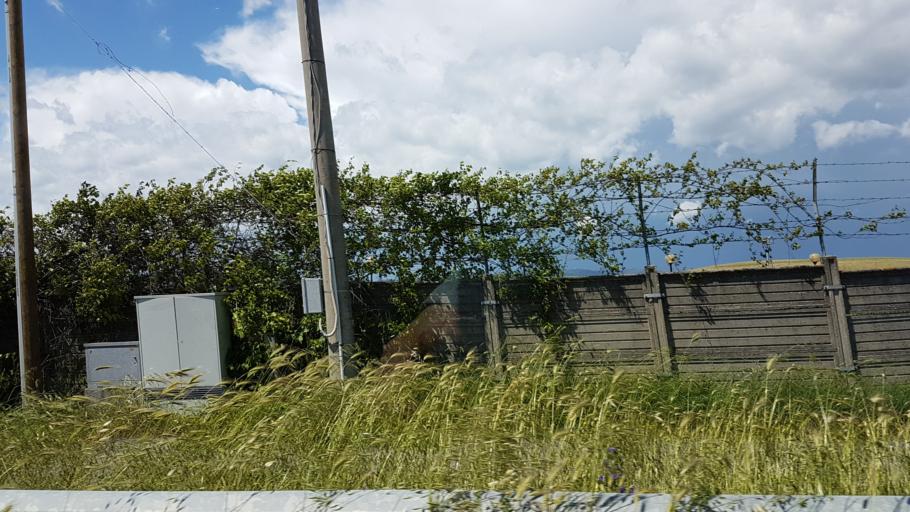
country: IT
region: Tuscany
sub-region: Provincia di Livorno
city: Rosignano Marittimo
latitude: 43.4400
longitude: 10.4947
